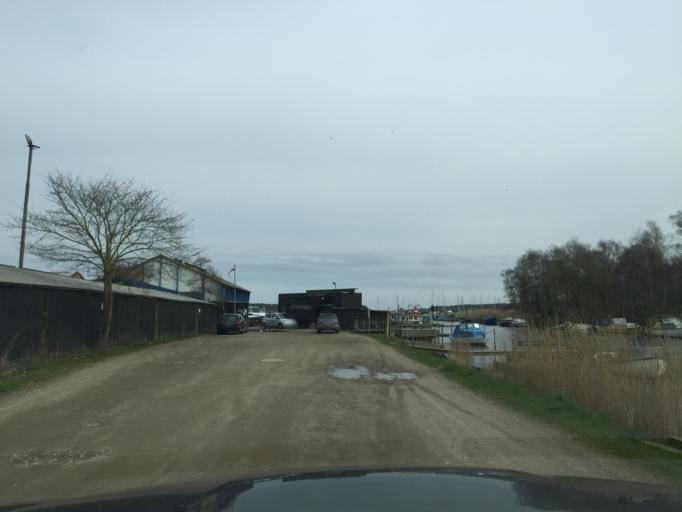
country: DK
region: South Denmark
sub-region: Kolding Kommune
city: Kolding
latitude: 55.4892
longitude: 9.4935
